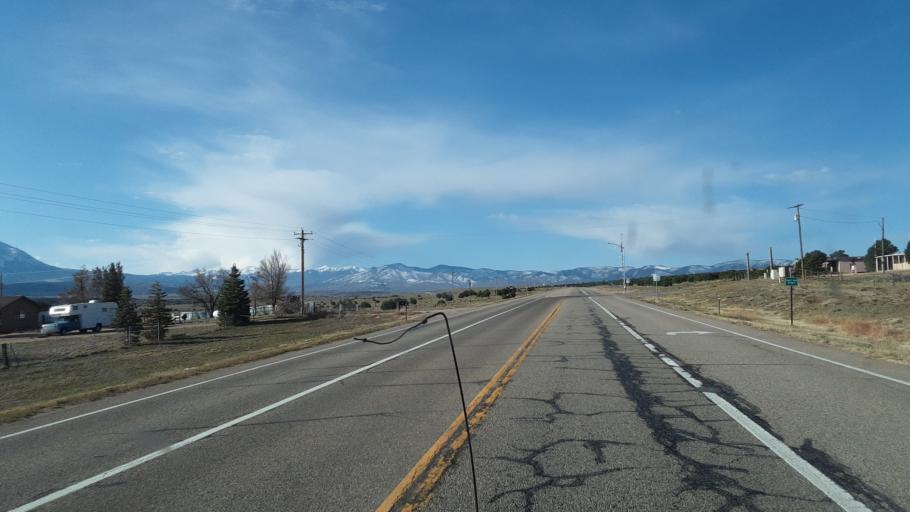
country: US
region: Colorado
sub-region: Huerfano County
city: Walsenburg
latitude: 37.5805
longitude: -104.9074
